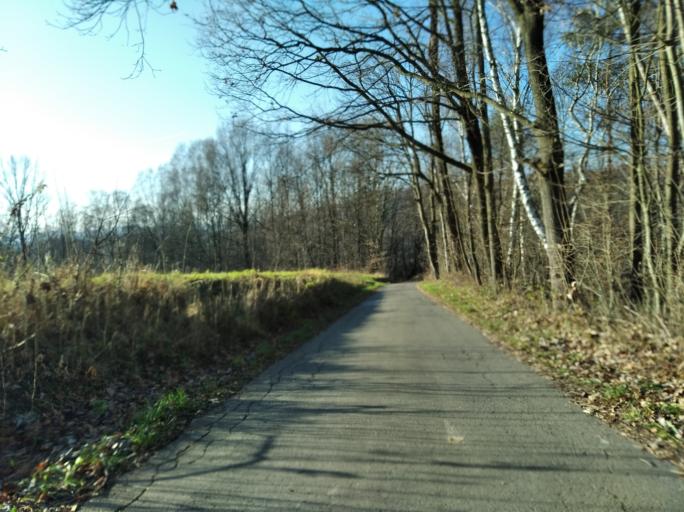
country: PL
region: Subcarpathian Voivodeship
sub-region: Powiat strzyzowski
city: Strzyzow
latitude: 49.8781
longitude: 21.8247
